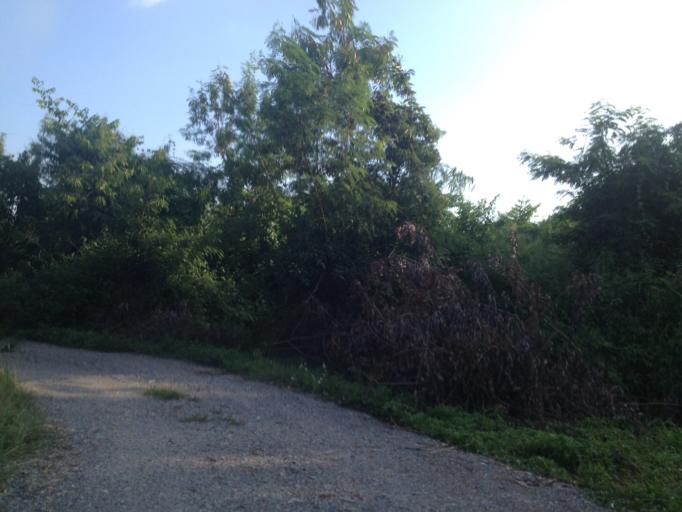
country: TH
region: Chiang Mai
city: Hang Dong
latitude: 18.6827
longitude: 98.9006
